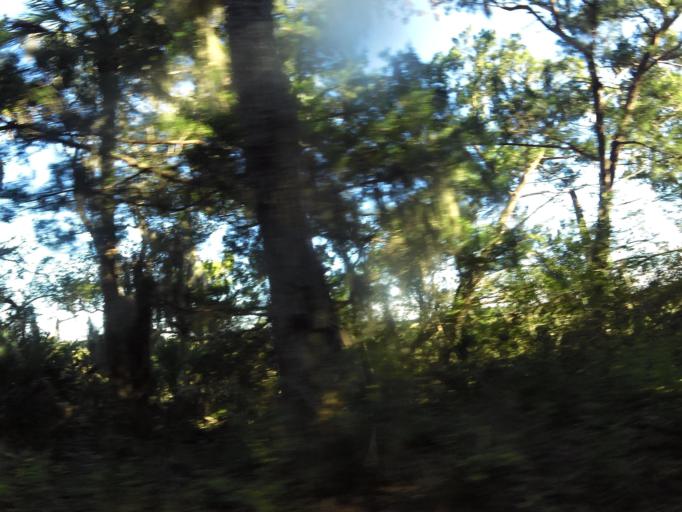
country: US
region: Florida
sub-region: Duval County
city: Atlantic Beach
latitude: 30.4106
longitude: -81.4301
